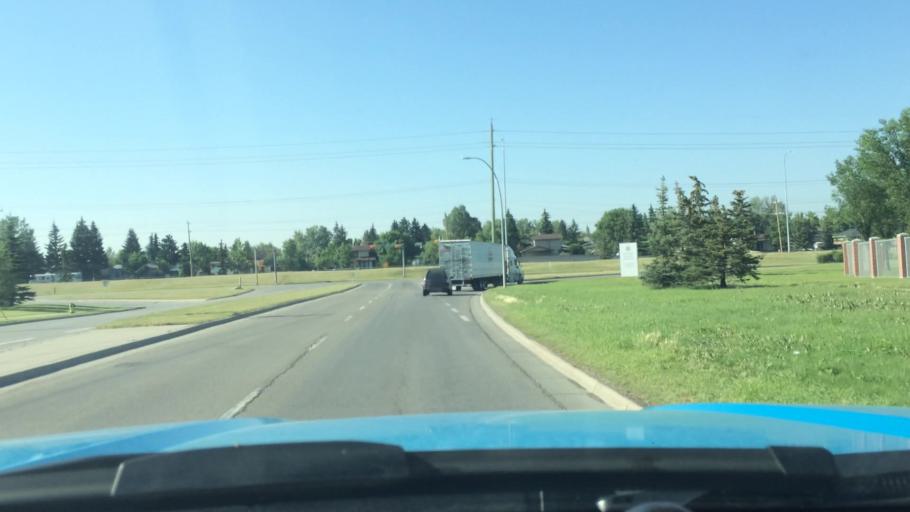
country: CA
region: Alberta
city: Calgary
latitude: 51.0973
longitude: -113.9661
